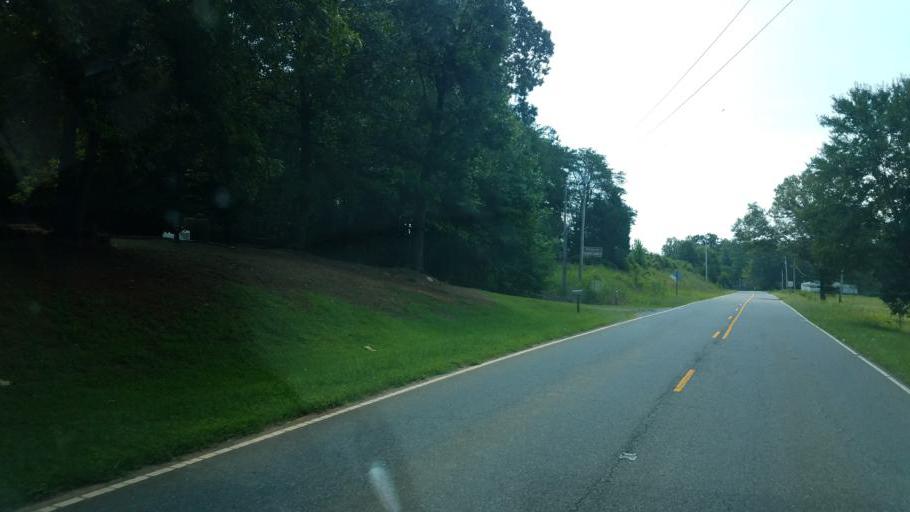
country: US
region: North Carolina
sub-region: Gaston County
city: Cherryville
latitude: 35.4176
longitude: -81.4095
